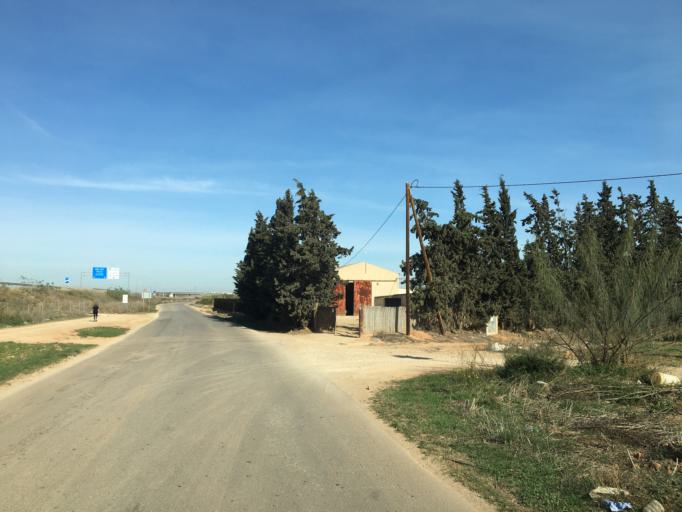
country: ES
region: Murcia
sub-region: Murcia
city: Cartagena
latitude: 37.6566
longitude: -1.0238
